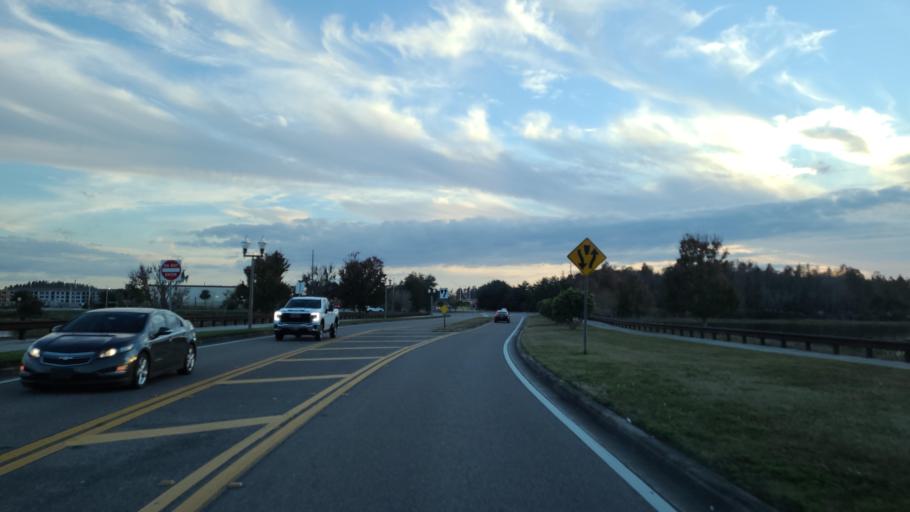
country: US
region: Florida
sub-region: Hillsborough County
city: Cheval
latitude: 28.1974
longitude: -82.5243
